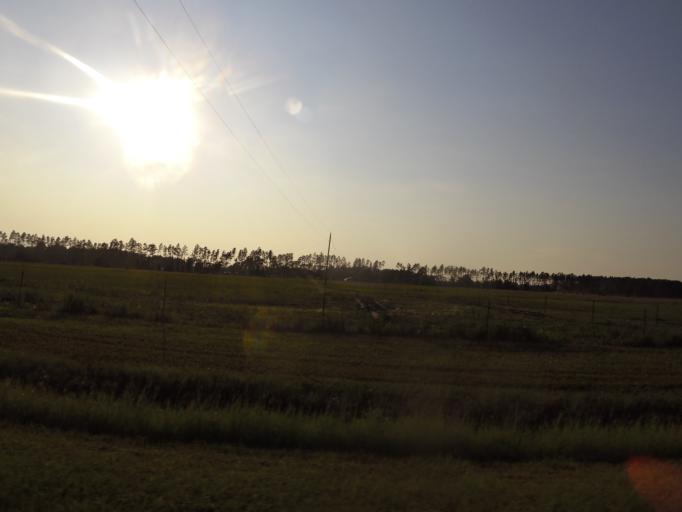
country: US
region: Florida
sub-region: Nassau County
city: Callahan
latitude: 30.5286
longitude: -81.9912
